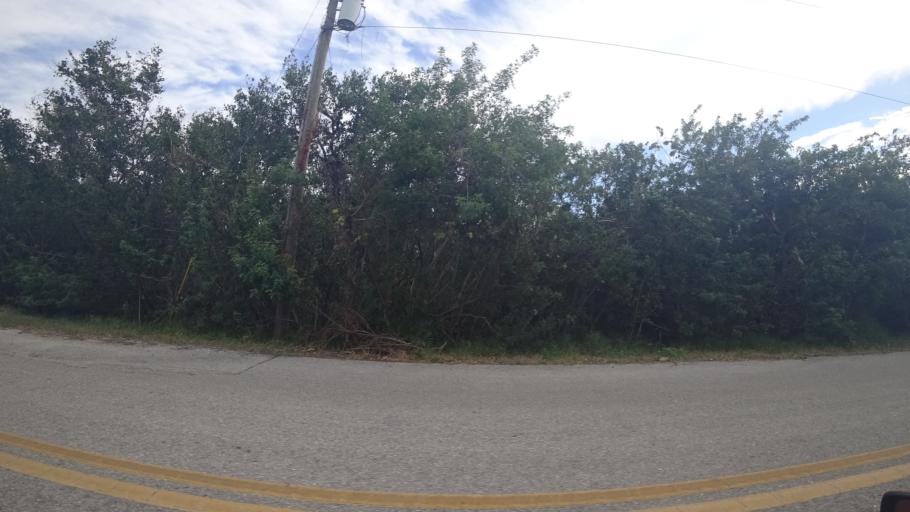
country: US
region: Florida
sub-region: Manatee County
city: West Bradenton
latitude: 27.4718
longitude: -82.6405
